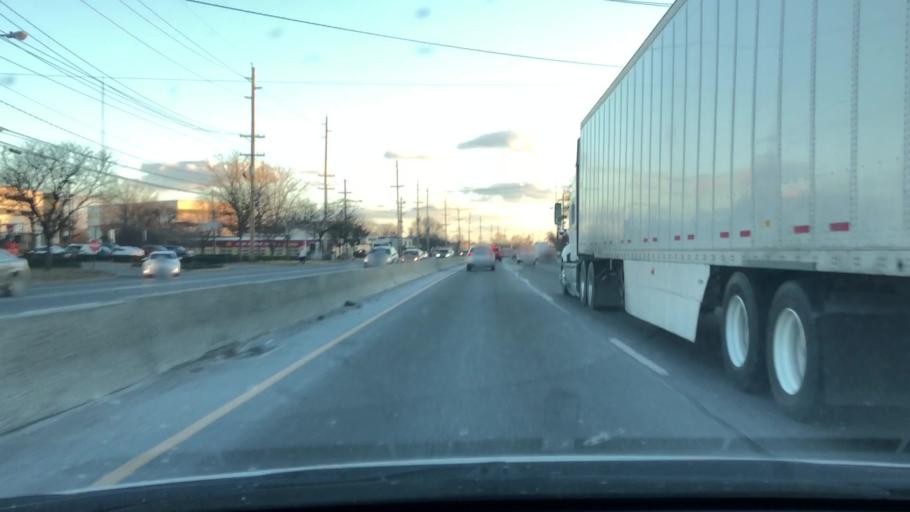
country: US
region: New Jersey
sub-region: Bergen County
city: Paramus
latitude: 40.9561
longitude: -74.0739
